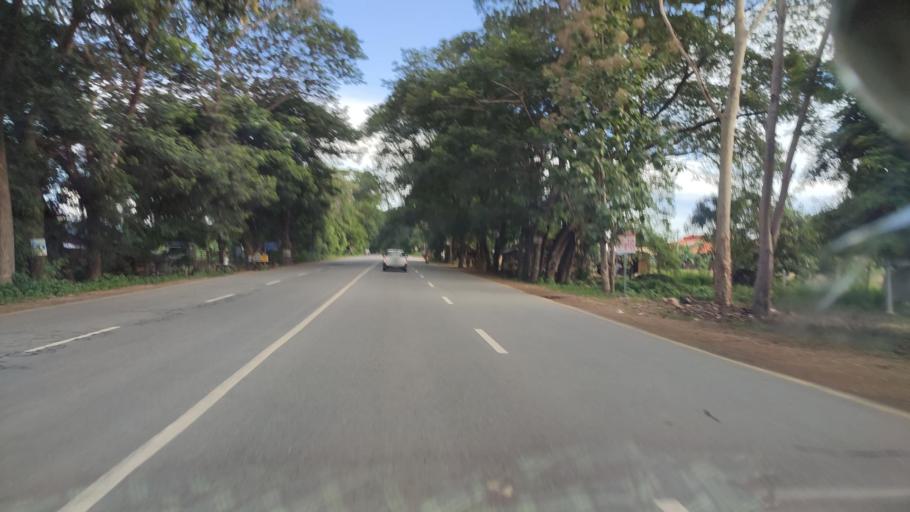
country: MM
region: Mandalay
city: Yamethin
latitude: 20.2227
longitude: 96.1800
